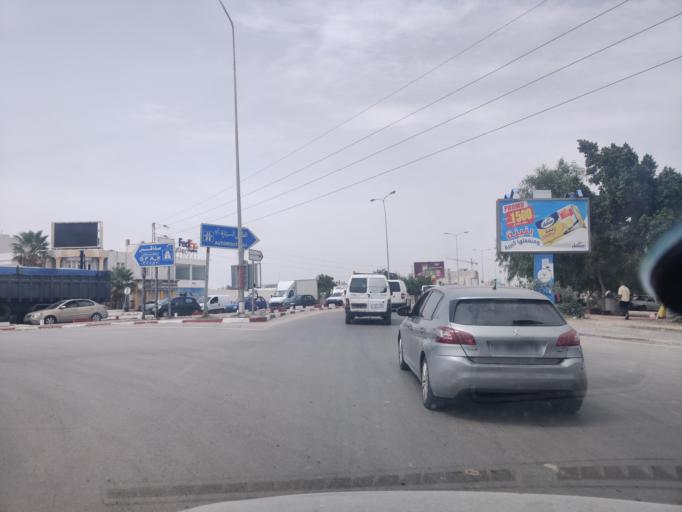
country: TN
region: Susah
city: Hammam Sousse
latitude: 35.8340
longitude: 10.5896
